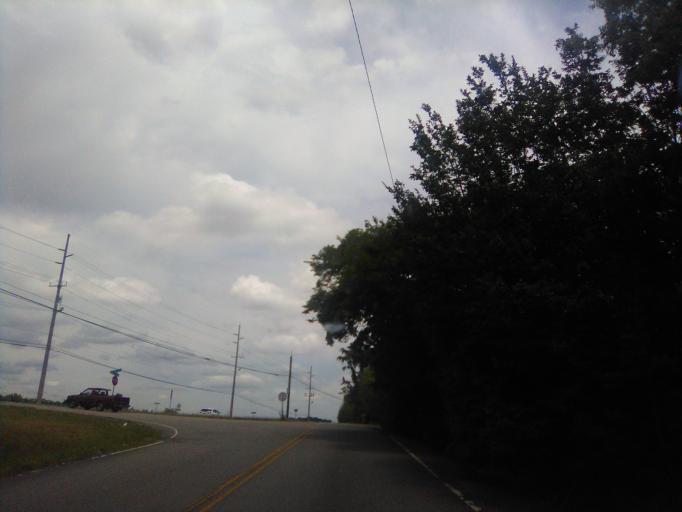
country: US
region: Tennessee
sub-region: Davidson County
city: Belle Meade
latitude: 36.1330
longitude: -86.8915
